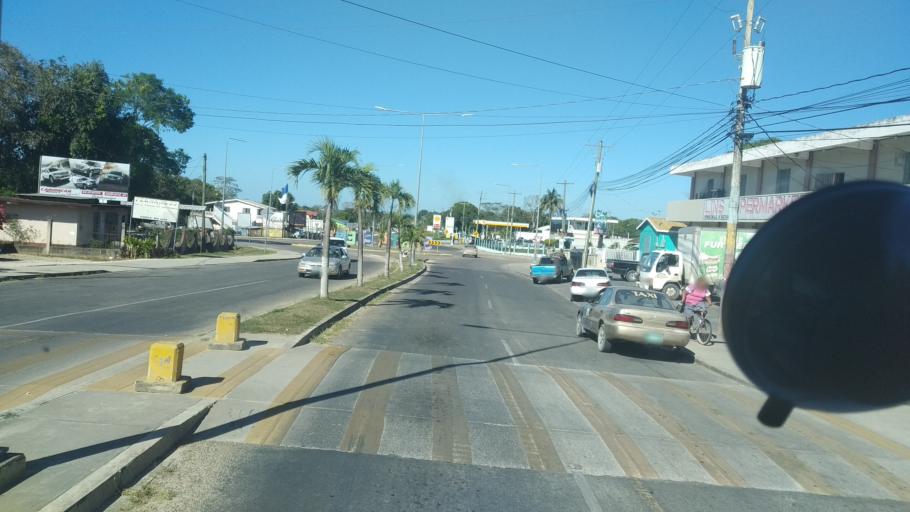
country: BZ
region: Cayo
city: San Ignacio
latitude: 17.1662
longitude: -89.0545
